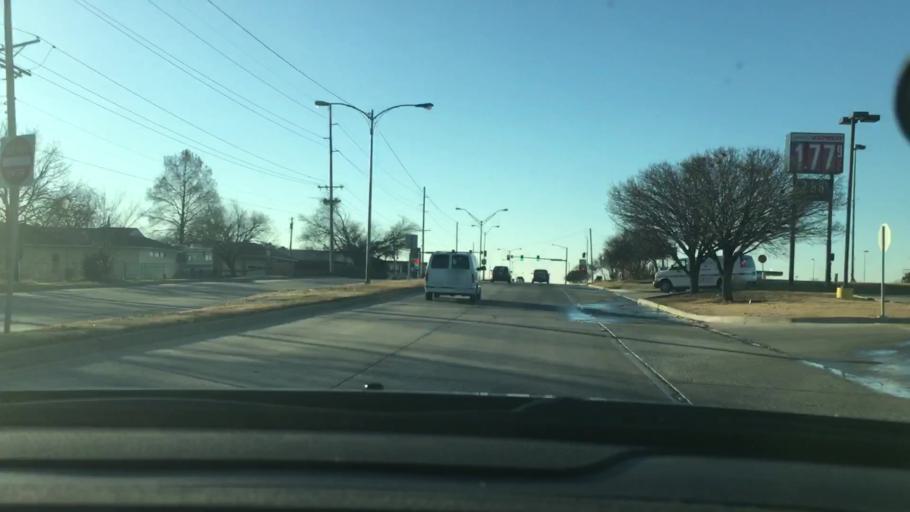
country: US
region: Oklahoma
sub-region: Carter County
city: Ardmore
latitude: 34.1946
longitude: -97.1432
